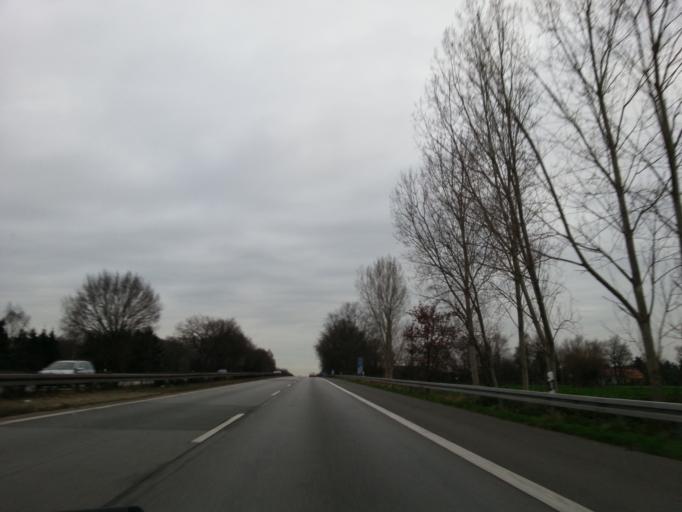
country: DE
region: North Rhine-Westphalia
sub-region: Regierungsbezirk Dusseldorf
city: Dinslaken
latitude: 51.5674
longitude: 6.8034
